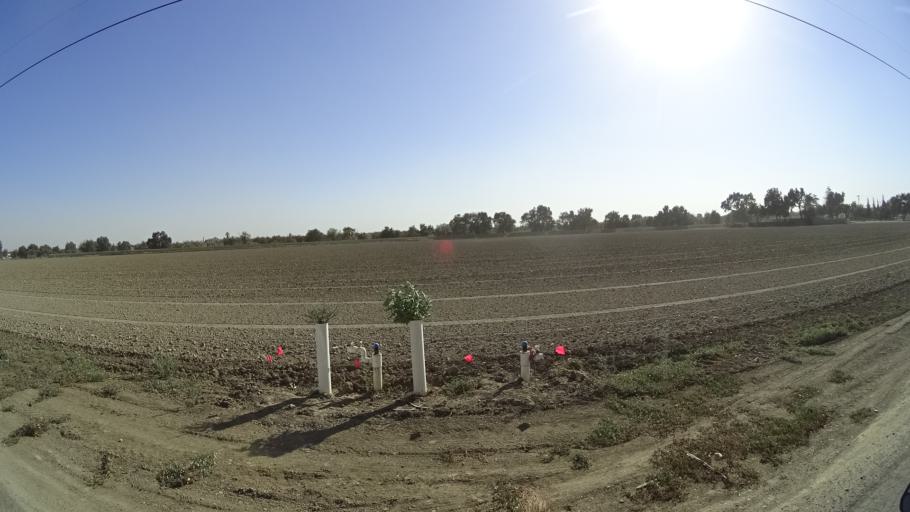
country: US
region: California
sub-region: Yolo County
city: Woodland
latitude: 38.7362
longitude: -121.8019
